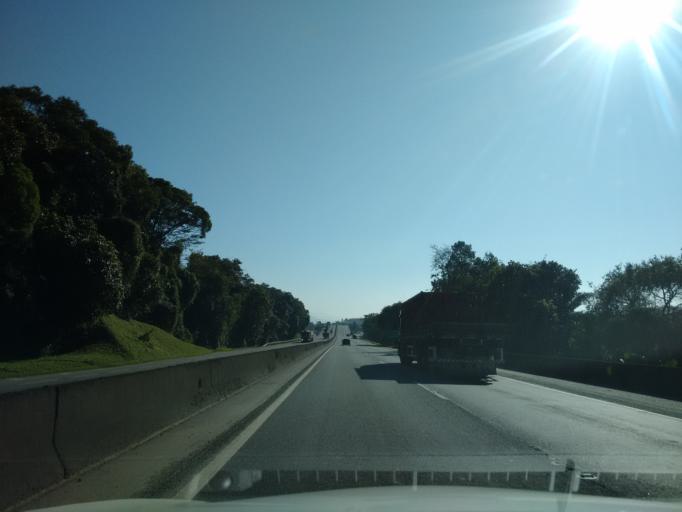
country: BR
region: Santa Catarina
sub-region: Joinville
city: Joinville
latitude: -26.2076
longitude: -48.9149
